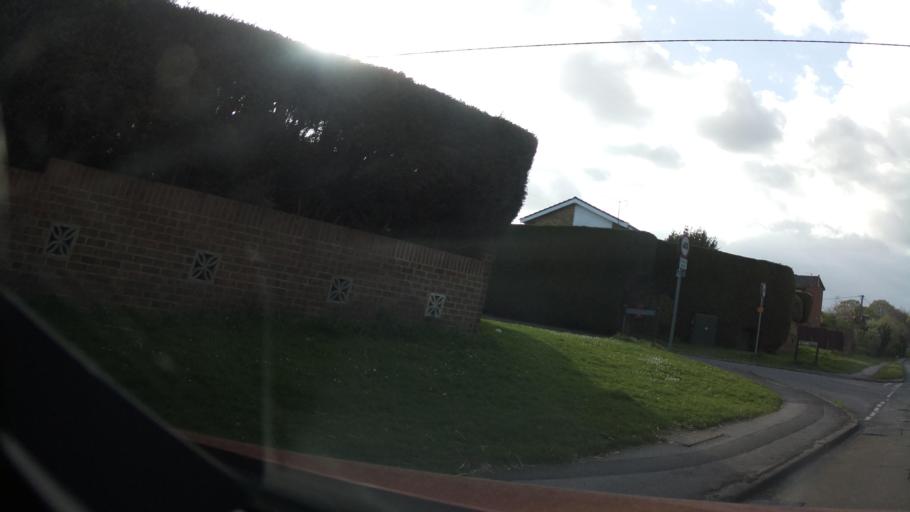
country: GB
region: England
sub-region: Hampshire
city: Colden Common
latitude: 50.9689
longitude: -1.2989
